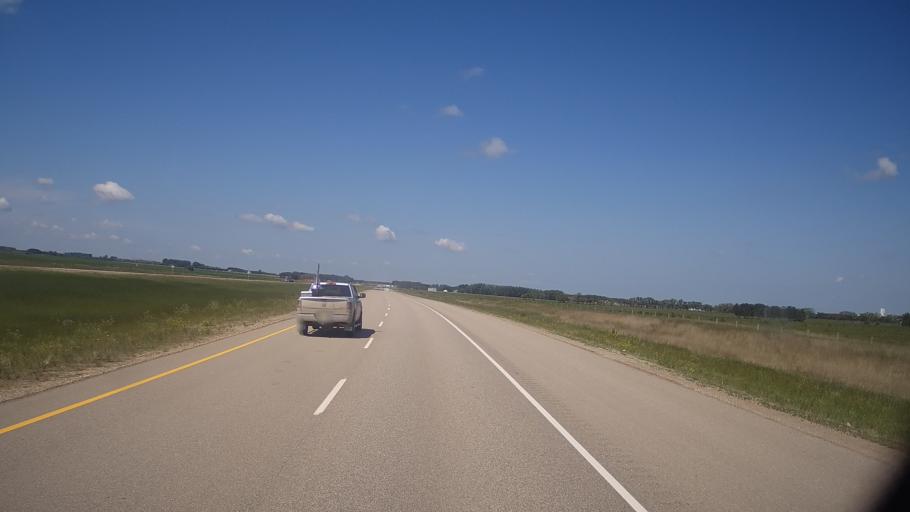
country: CA
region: Saskatchewan
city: Saskatoon
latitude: 52.0122
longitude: -106.3670
